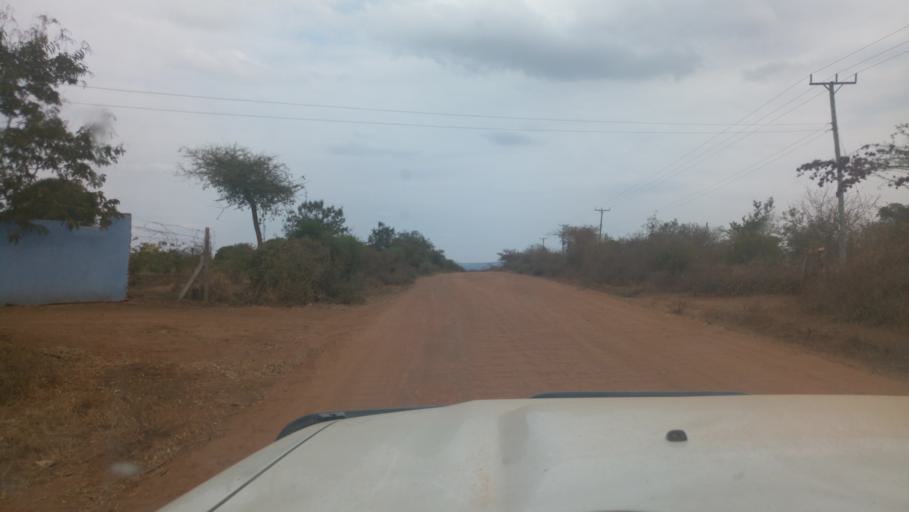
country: KE
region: Kitui
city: Kitui
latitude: -1.6240
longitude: 37.9091
